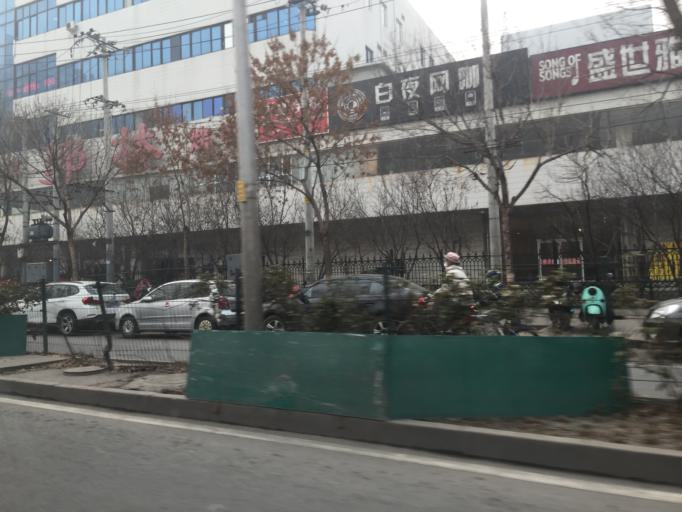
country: CN
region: Beijing
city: Qinghe
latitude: 40.0009
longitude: 116.3463
